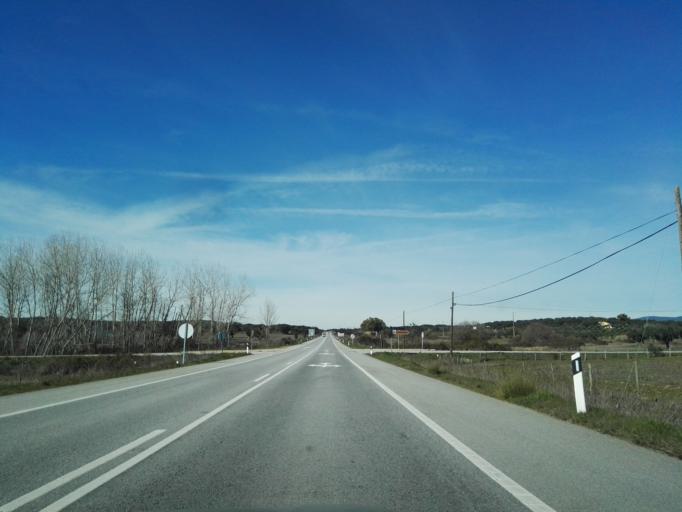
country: PT
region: Portalegre
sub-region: Arronches
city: Arronches
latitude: 39.1598
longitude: -7.3207
